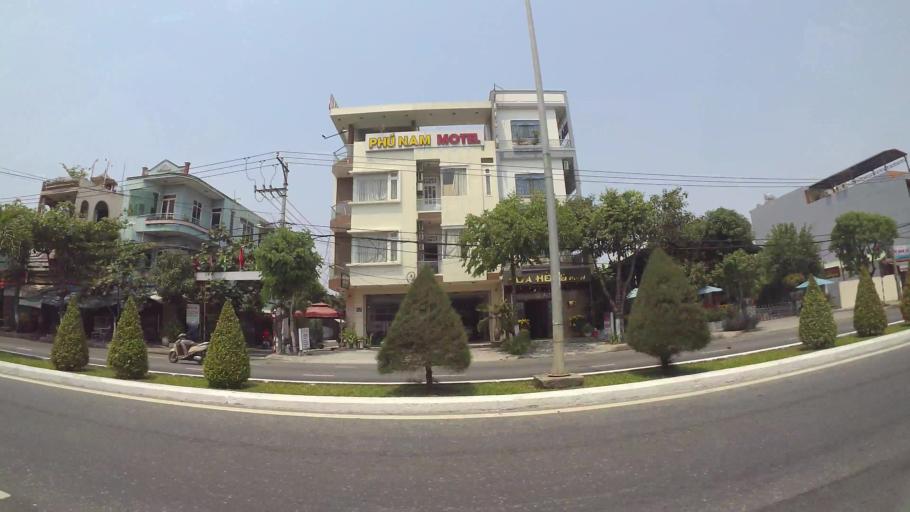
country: VN
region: Da Nang
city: Cam Le
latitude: 16.0233
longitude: 108.2151
